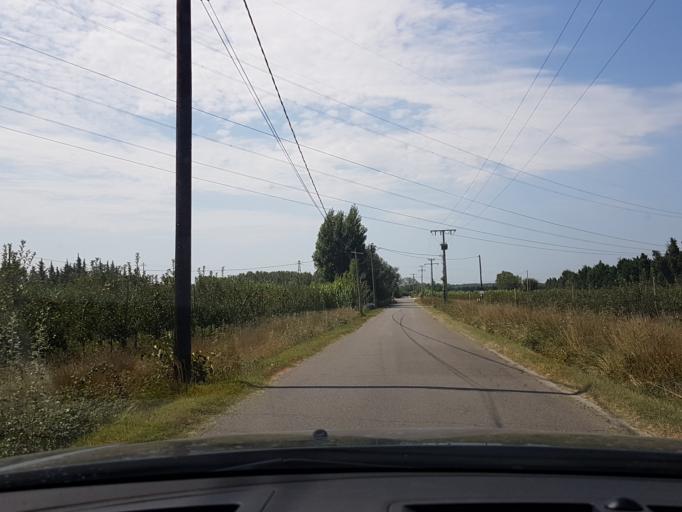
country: FR
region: Provence-Alpes-Cote d'Azur
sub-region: Departement des Bouches-du-Rhone
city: Molleges
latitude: 43.8051
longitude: 4.8909
